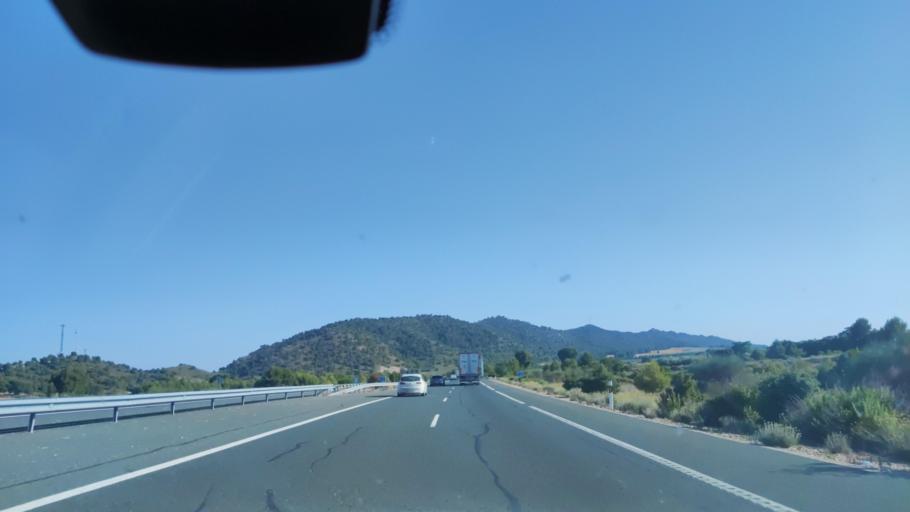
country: ES
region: Castille-La Mancha
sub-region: Provincia de Albacete
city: Tobarra
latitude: 38.6810
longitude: -1.6700
